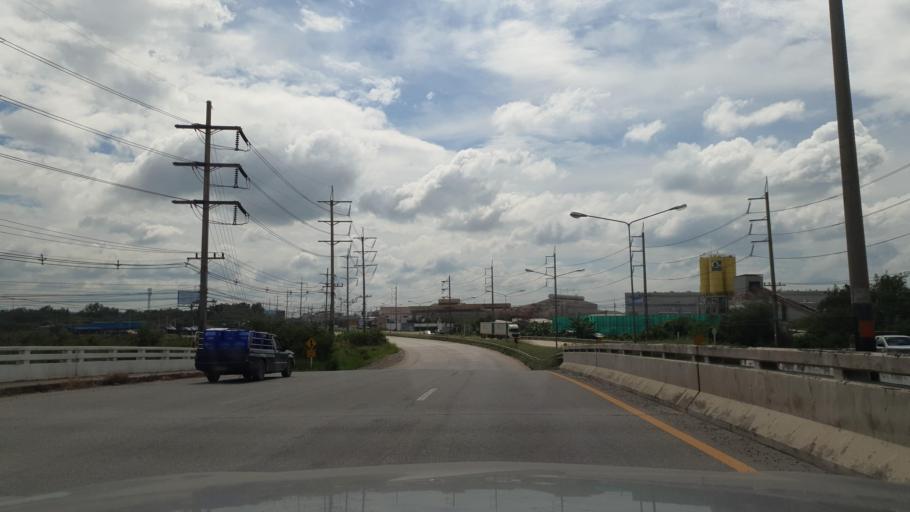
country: TH
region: Chachoengsao
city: Bang Pakong
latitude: 13.5537
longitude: 100.9913
